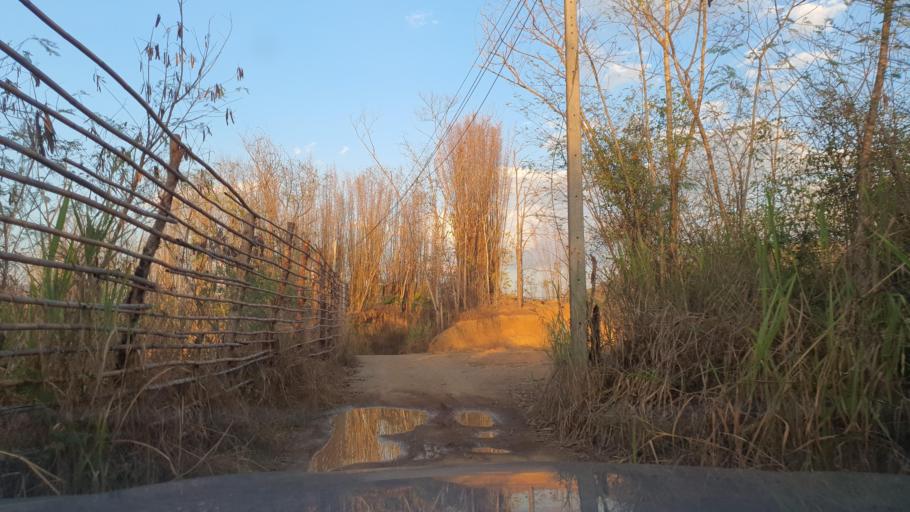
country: TH
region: Chiang Mai
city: Hang Dong
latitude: 18.7314
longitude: 98.8808
